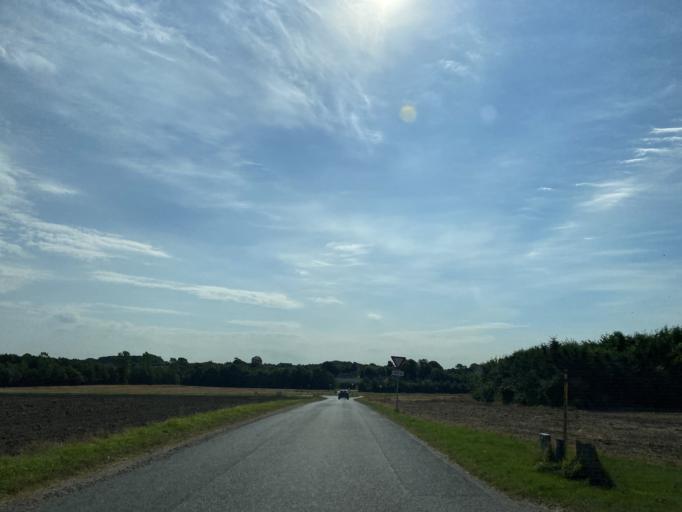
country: DK
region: Central Jutland
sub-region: Favrskov Kommune
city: Ulstrup
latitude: 56.3236
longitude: 9.7663
